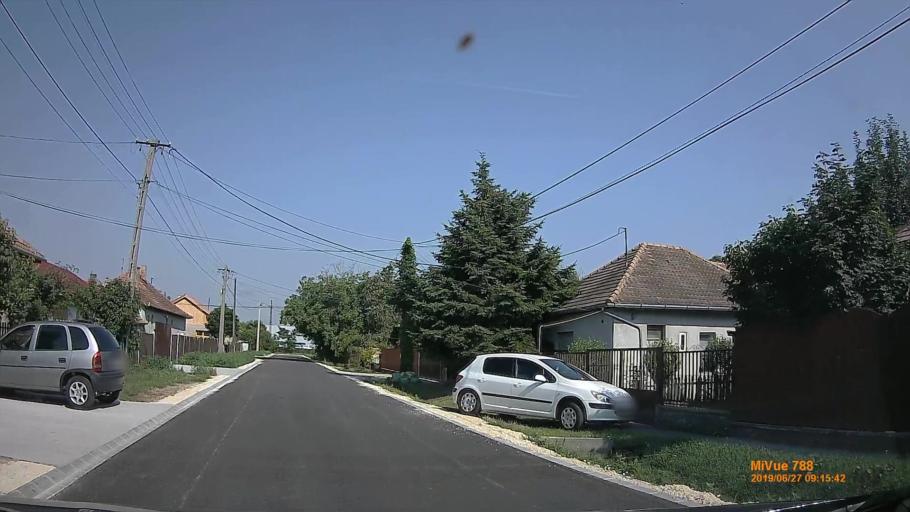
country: HU
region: Pest
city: Ullo
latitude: 47.3954
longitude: 19.3570
